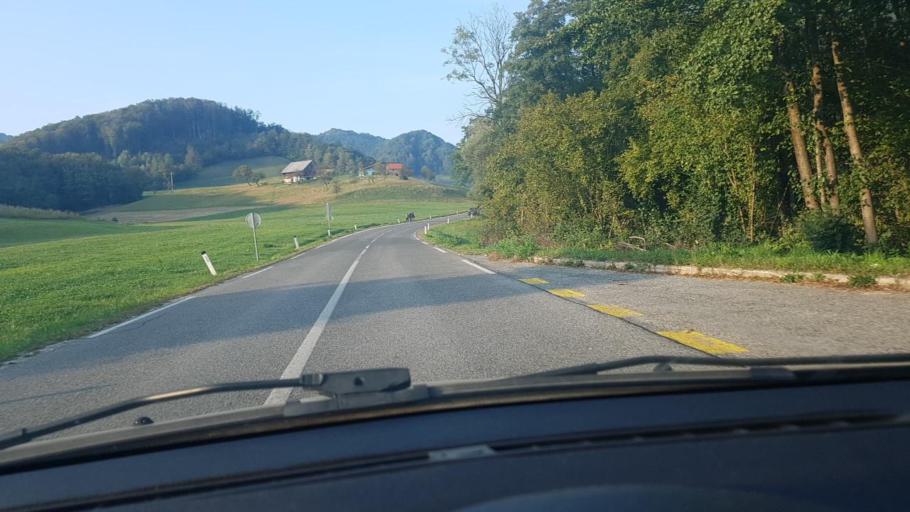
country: SI
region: Rogatec
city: Rogatec
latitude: 46.2523
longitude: 15.7011
